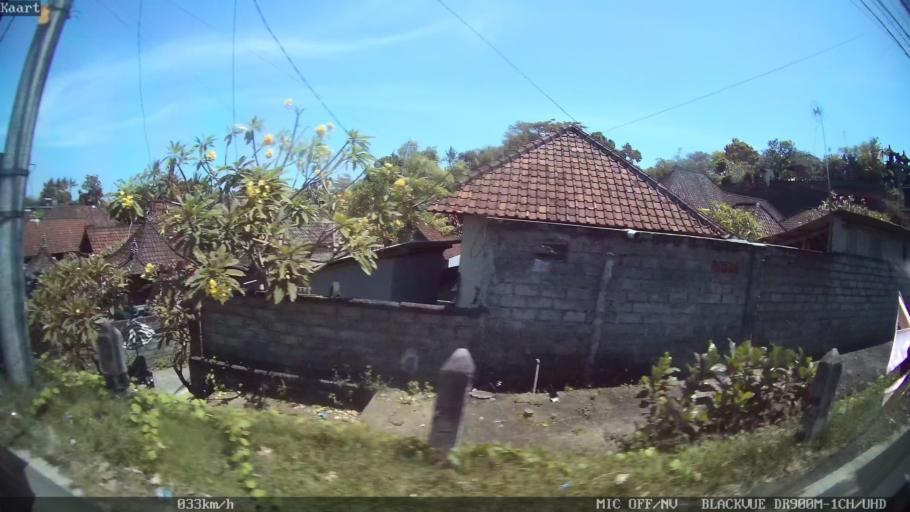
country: ID
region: Bali
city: Klungkung
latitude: -8.5779
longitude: 115.3513
